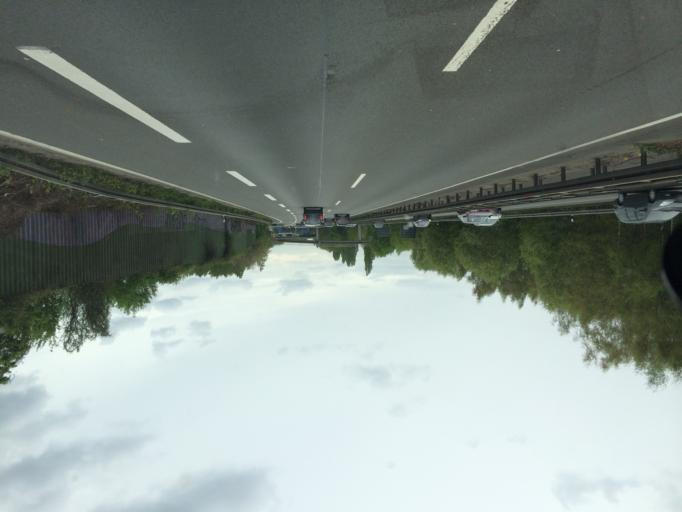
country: DE
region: North Rhine-Westphalia
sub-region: Regierungsbezirk Arnsberg
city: Herne
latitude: 51.5276
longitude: 7.2079
